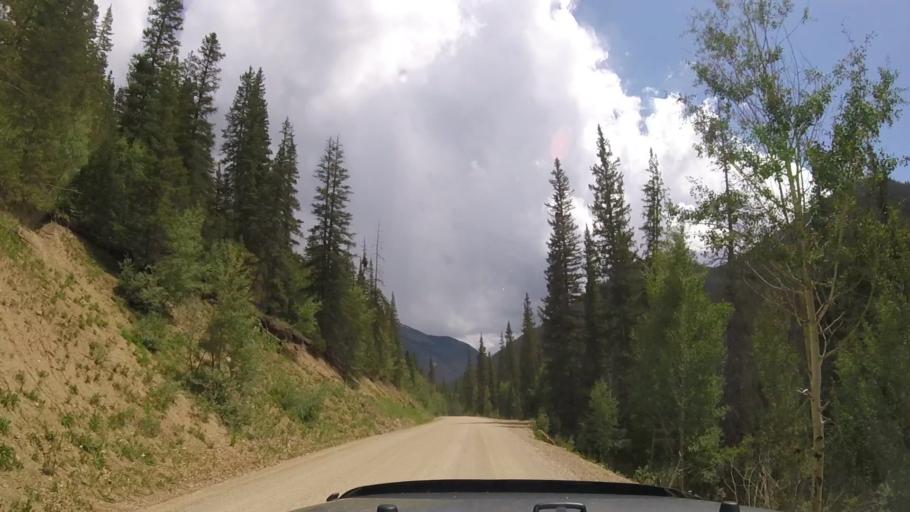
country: US
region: Colorado
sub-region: San Juan County
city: Silverton
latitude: 37.8328
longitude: -107.6717
